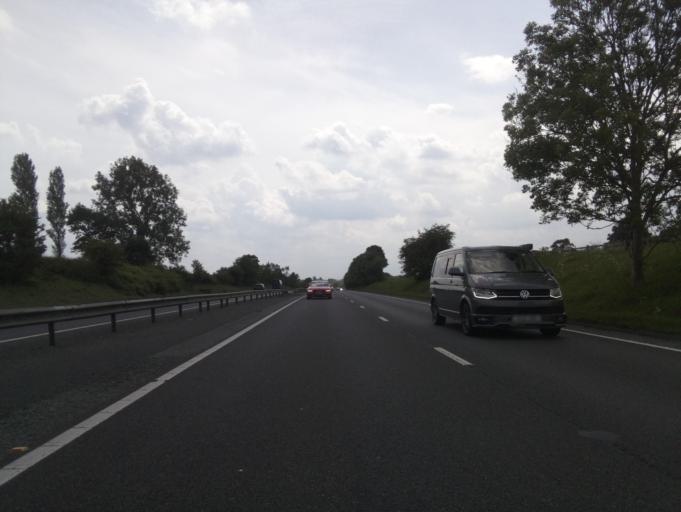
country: GB
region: England
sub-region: North Yorkshire
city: Thirsk
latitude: 54.3009
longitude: -1.3369
